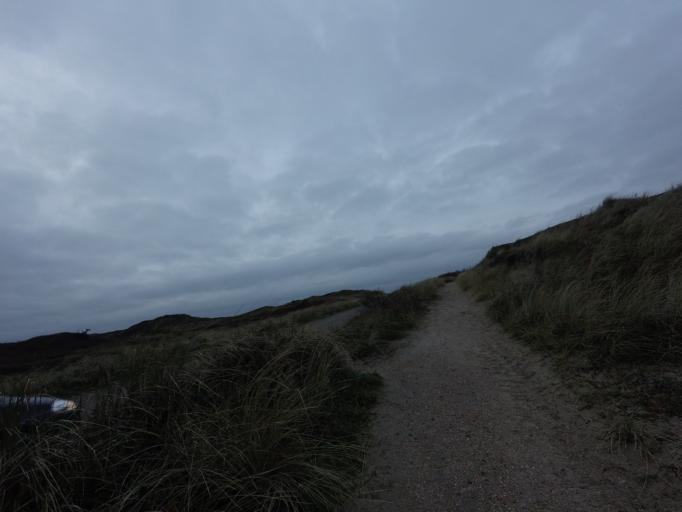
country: NL
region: North Holland
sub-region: Gemeente Texel
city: Den Burg
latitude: 53.0801
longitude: 4.7426
